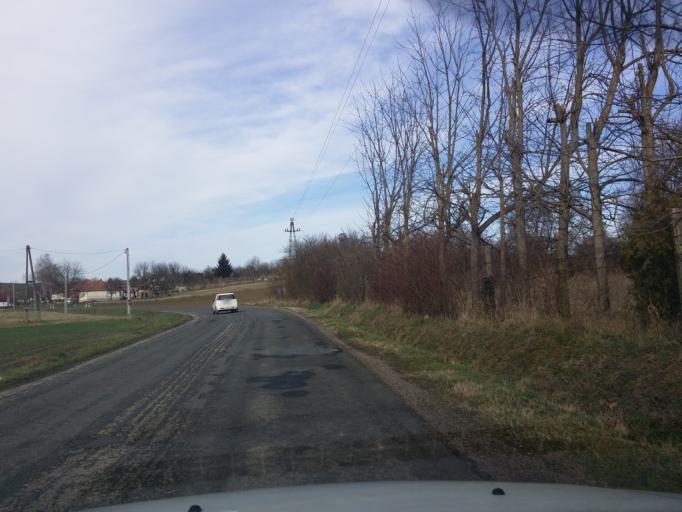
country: HU
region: Baranya
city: Villany
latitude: 45.8800
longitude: 18.4353
